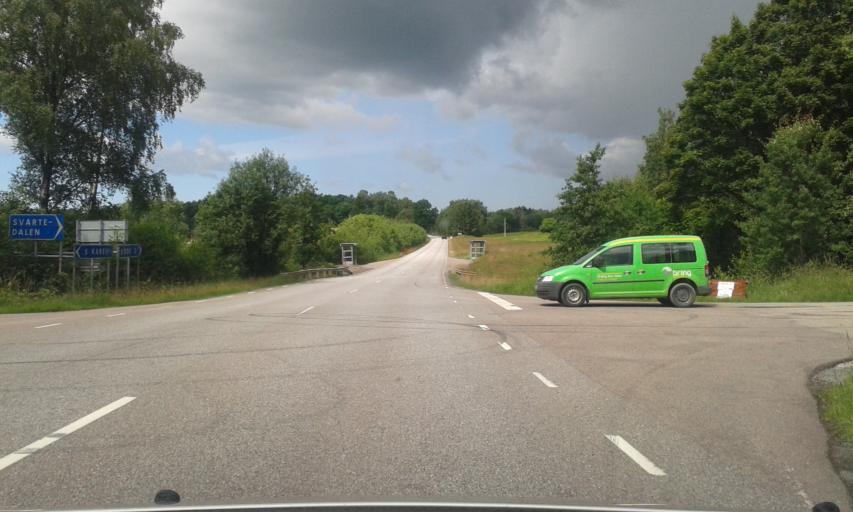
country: SE
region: Vaestra Goetaland
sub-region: Kungalvs Kommun
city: Kode
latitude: 57.9355
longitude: 11.8771
